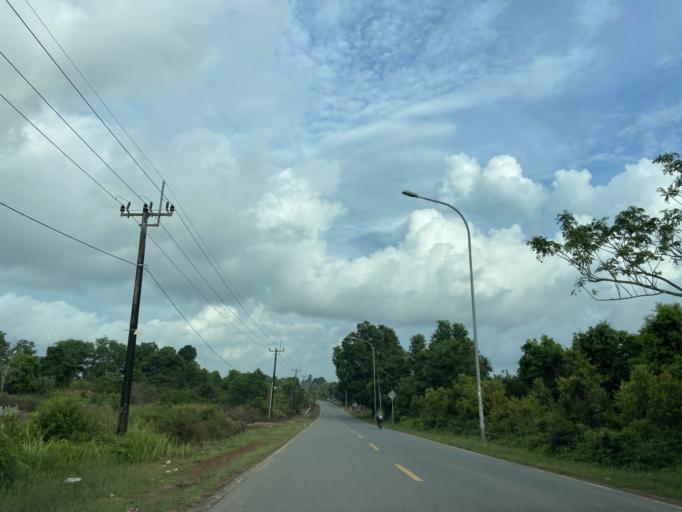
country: ID
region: Riau Islands
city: Tanjungpinang
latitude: 0.9373
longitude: 104.0941
